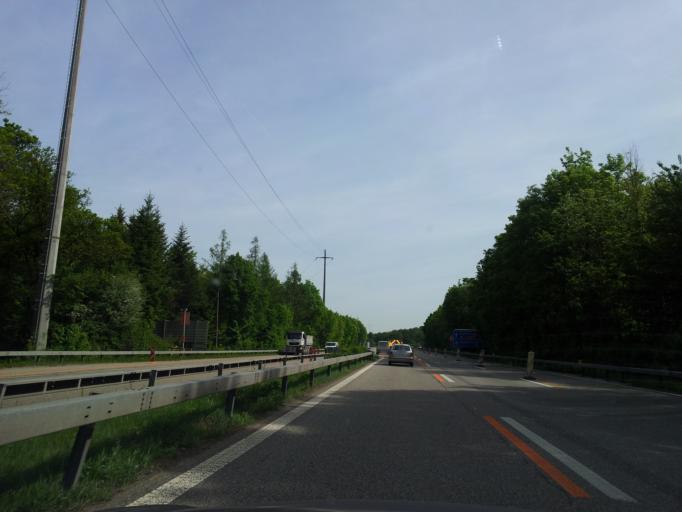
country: CH
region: Zurich
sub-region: Bezirk Buelach
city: Buelach / Niederflachs
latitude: 47.5243
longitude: 8.5291
